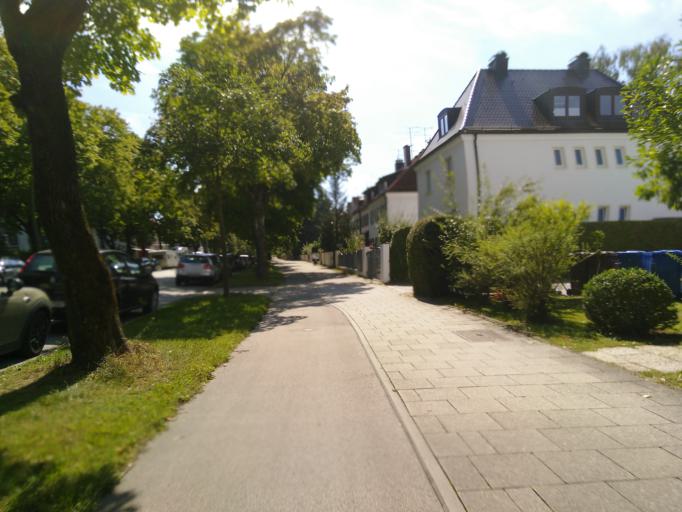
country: DE
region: Bavaria
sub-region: Upper Bavaria
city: Munich
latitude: 48.1032
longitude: 11.5728
